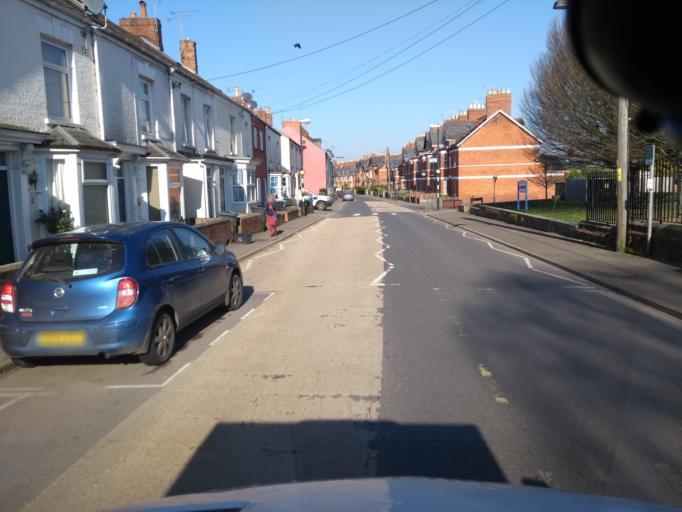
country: GB
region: England
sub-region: Somerset
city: Bishops Lydeard
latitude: 50.9795
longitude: -3.2317
